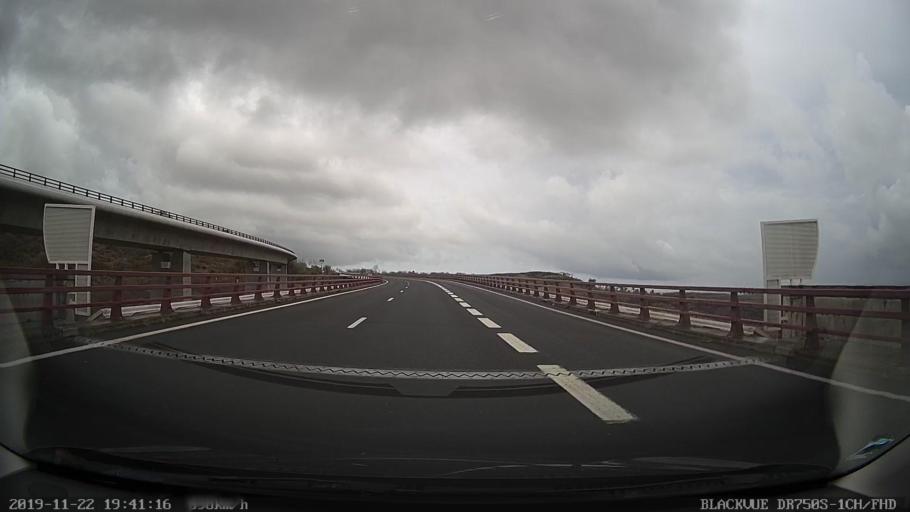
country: RE
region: Reunion
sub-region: Reunion
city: Saint-Paul
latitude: -21.0339
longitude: 55.2498
